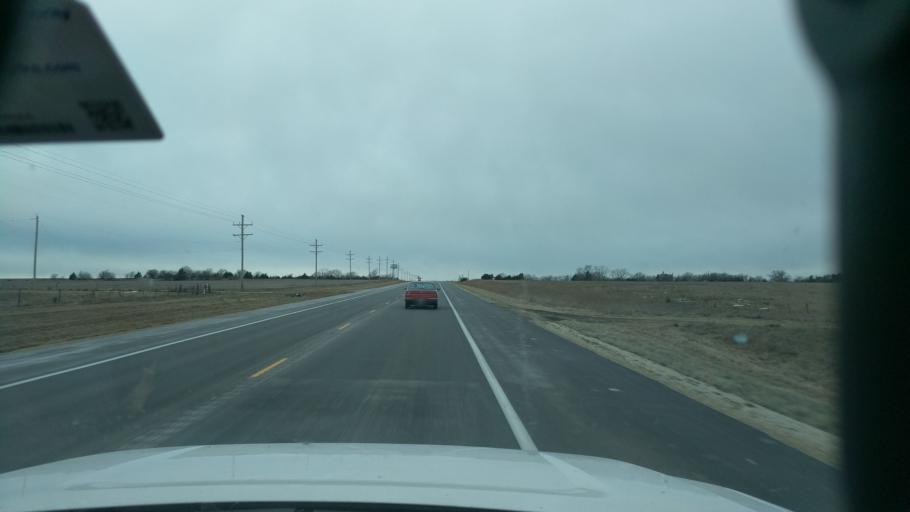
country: US
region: Kansas
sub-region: Marion County
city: Hillsboro
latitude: 38.3627
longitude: -97.2372
